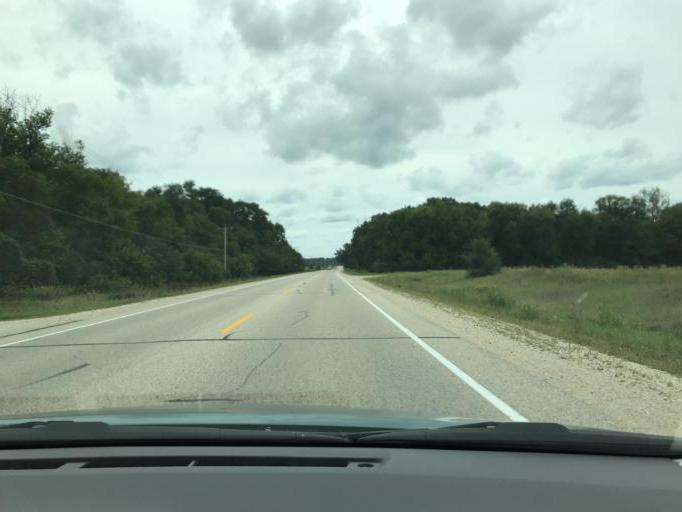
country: US
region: Wisconsin
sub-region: Racine County
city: Bohners Lake
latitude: 42.6238
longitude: -88.2411
